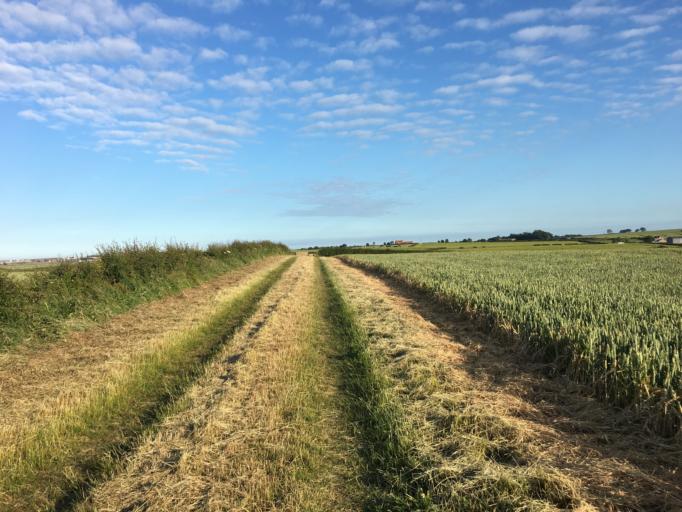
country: GB
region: England
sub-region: Northumberland
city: Bamburgh
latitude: 55.5996
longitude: -1.6973
